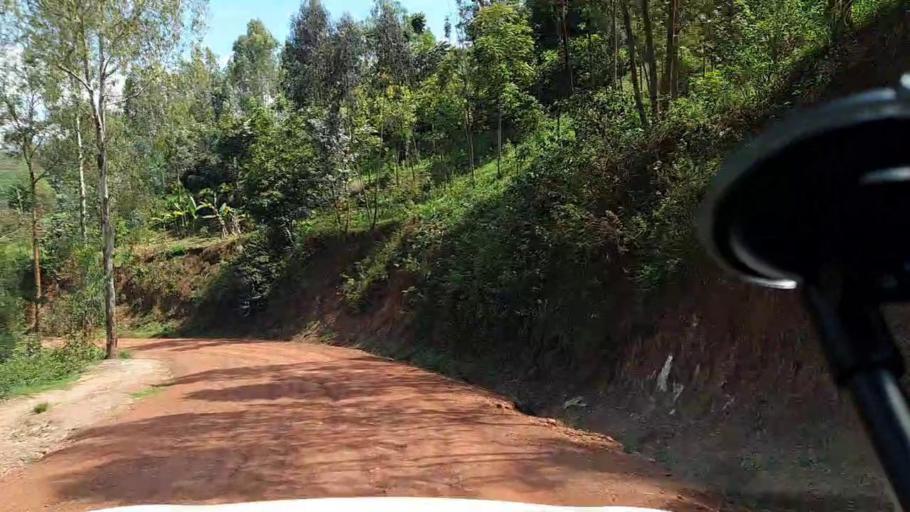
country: RW
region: Kigali
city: Kigali
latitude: -1.7983
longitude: 29.8867
